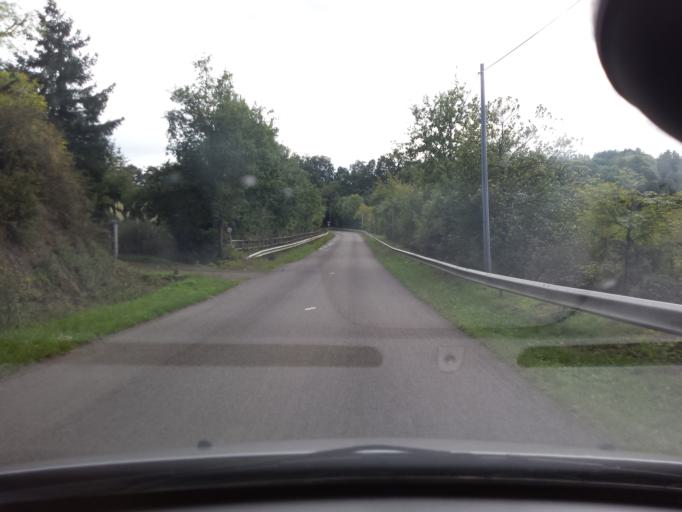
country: FR
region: Pays de la Loire
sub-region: Departement de la Vendee
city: Saint-Vincent-sur-Graon
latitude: 46.5243
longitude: -1.3975
